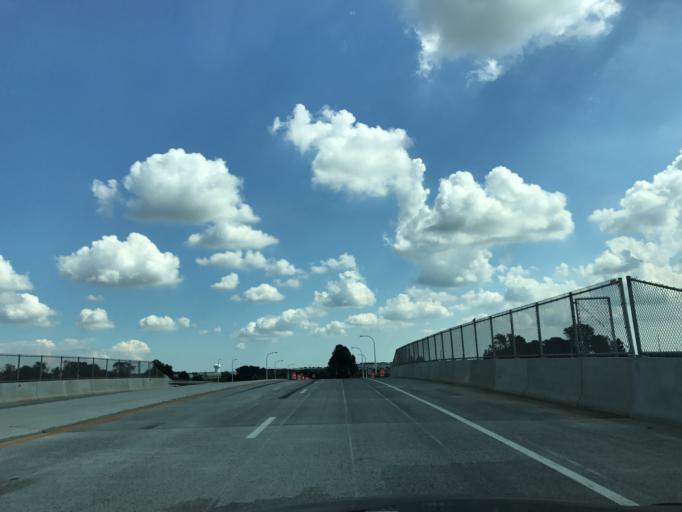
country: US
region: Delaware
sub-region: New Castle County
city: Middletown
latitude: 39.4452
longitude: -75.7524
